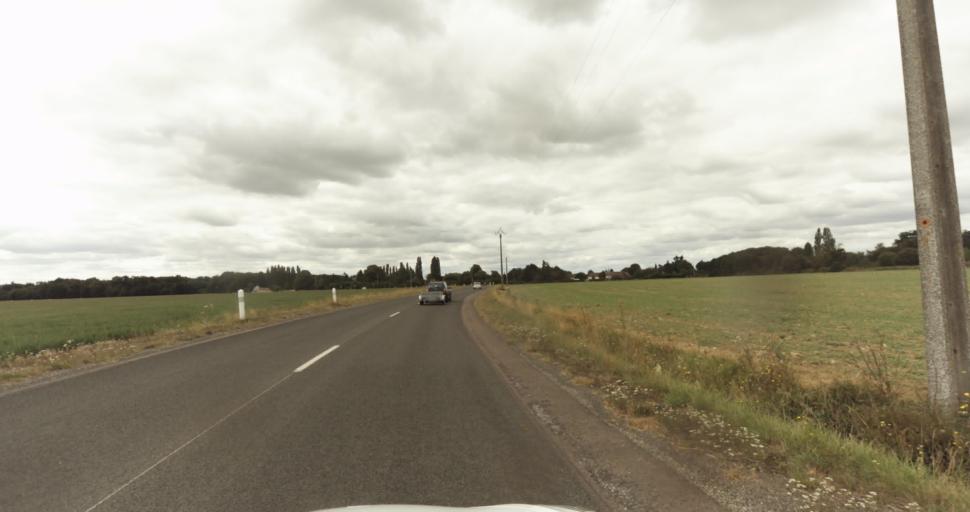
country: FR
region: Haute-Normandie
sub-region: Departement de l'Eure
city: La Madeleine-de-Nonancourt
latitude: 48.8334
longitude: 1.2291
